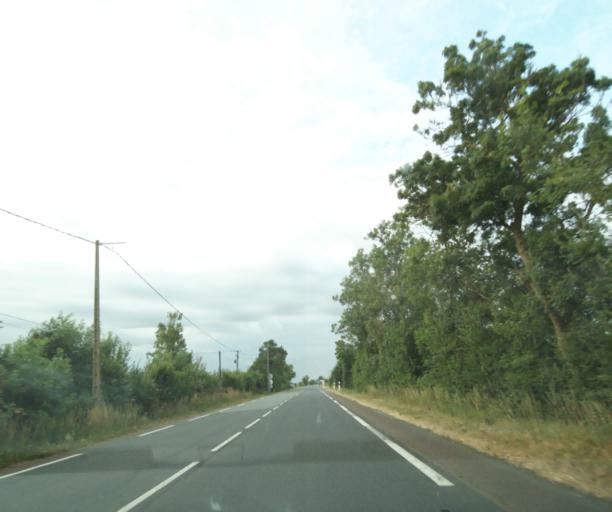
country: FR
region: Poitou-Charentes
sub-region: Departement de la Charente-Maritime
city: Marans
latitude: 46.3499
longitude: -0.9957
